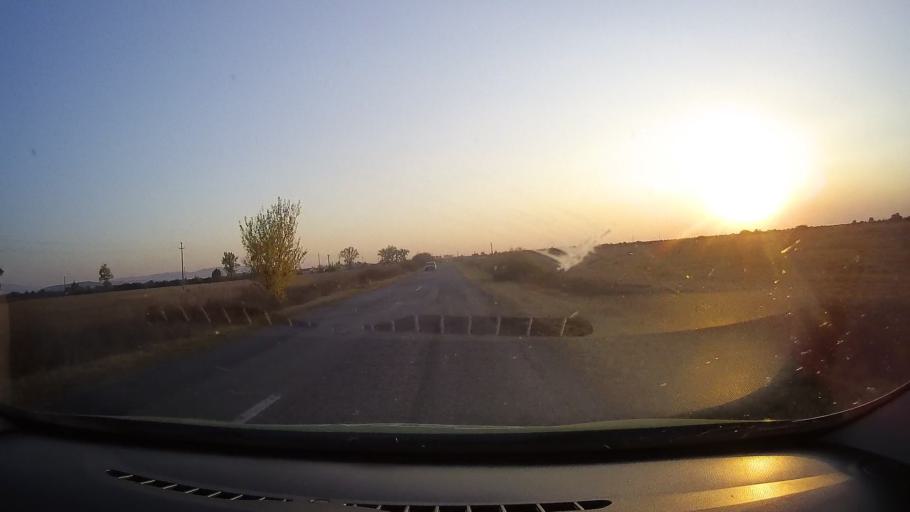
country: RO
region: Arad
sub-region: Comuna Seleus
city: Seleus
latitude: 46.3945
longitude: 21.7162
